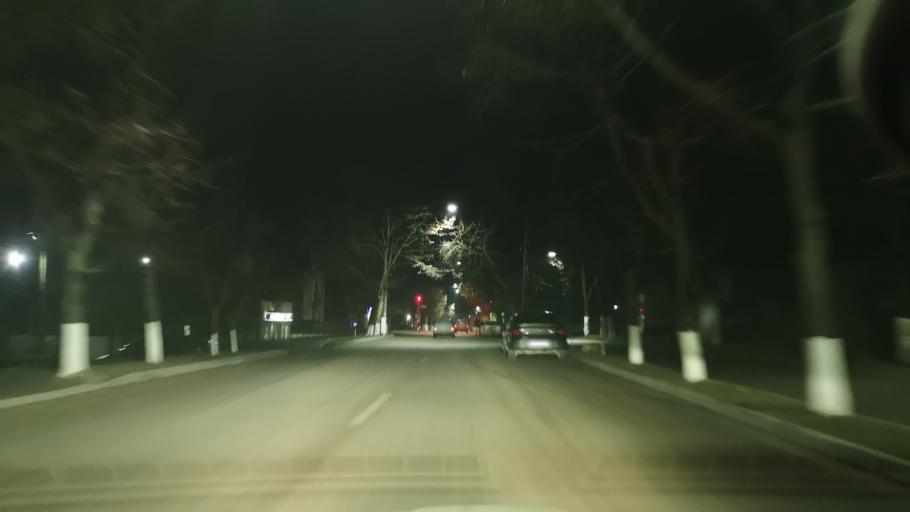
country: MD
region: Orhei
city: Orhei
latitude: 47.3881
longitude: 28.8241
